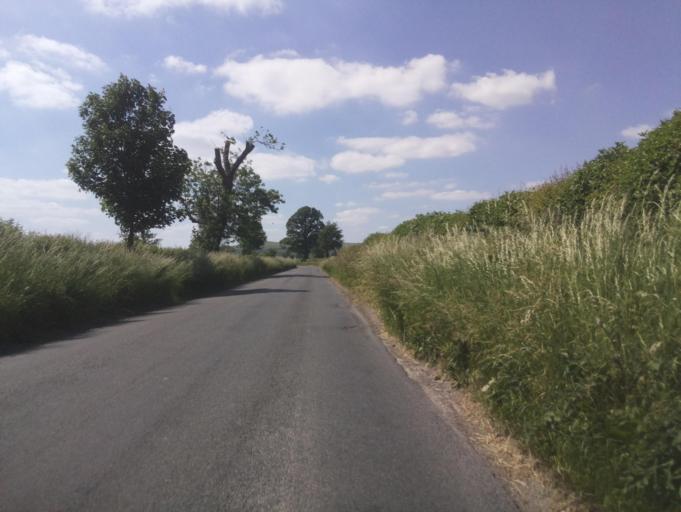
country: GB
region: England
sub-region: Wiltshire
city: Huish
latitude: 51.3581
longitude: -1.8081
